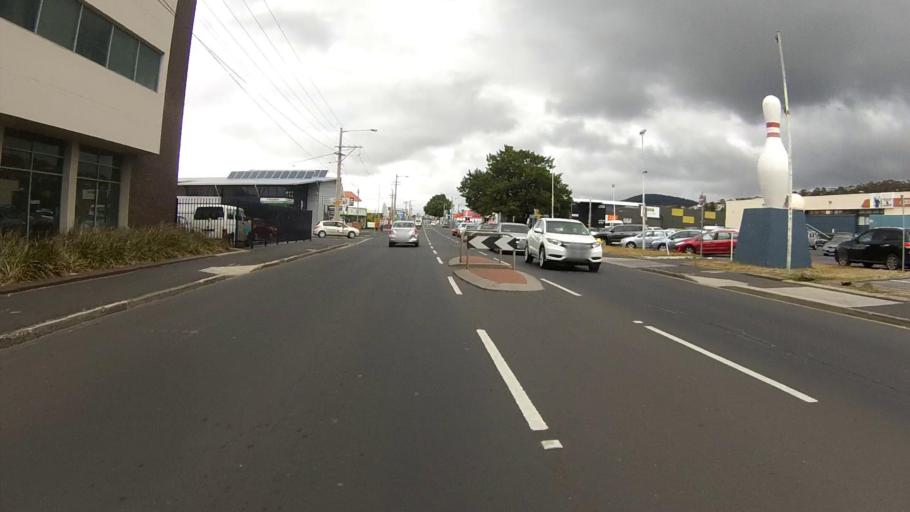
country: AU
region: Tasmania
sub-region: Glenorchy
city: Moonah
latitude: -42.8427
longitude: 147.2921
